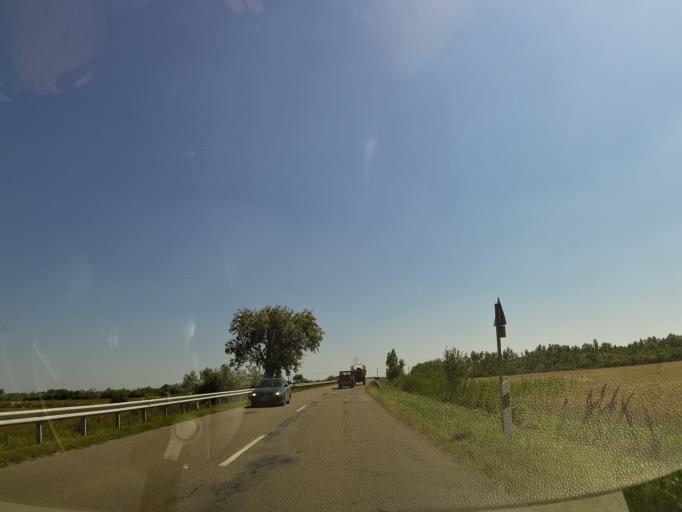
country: HU
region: Jasz-Nagykun-Szolnok
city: Fegyvernek
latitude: 47.2574
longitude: 20.5665
